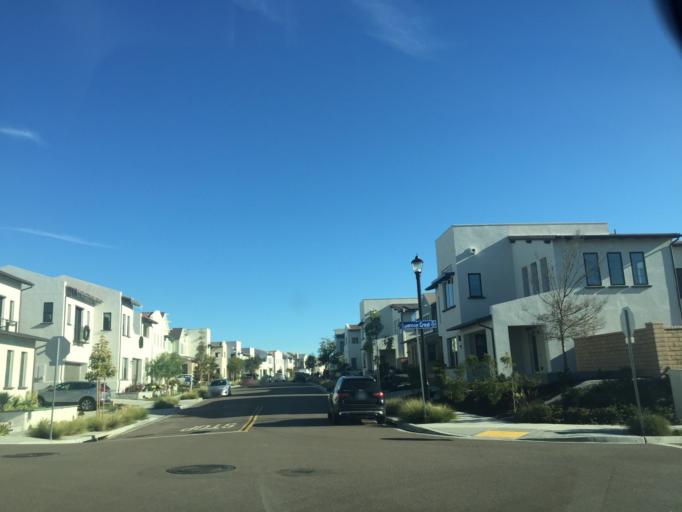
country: US
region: California
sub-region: San Diego County
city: Fairbanks Ranch
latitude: 32.9686
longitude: -117.1908
